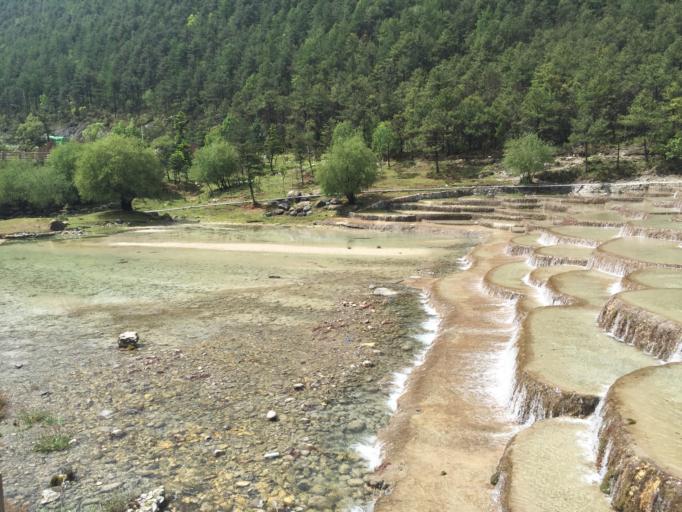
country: CN
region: Yunnan
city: Xiaqiaotou
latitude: 27.1298
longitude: 100.2405
